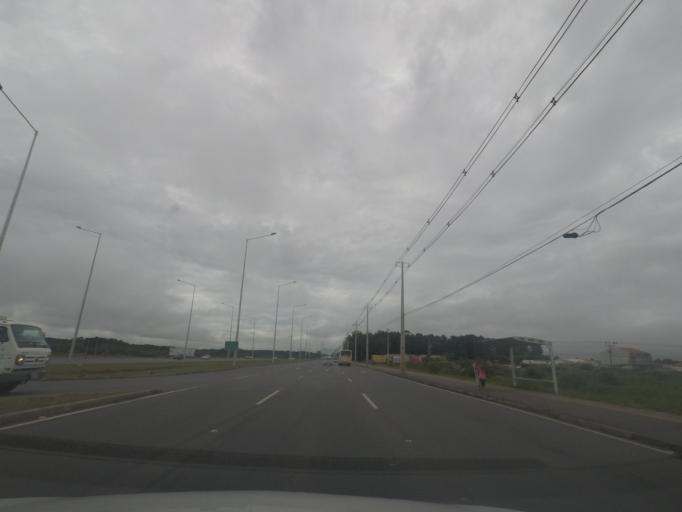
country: BR
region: Parana
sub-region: Pinhais
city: Pinhais
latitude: -25.4453
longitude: -49.1403
